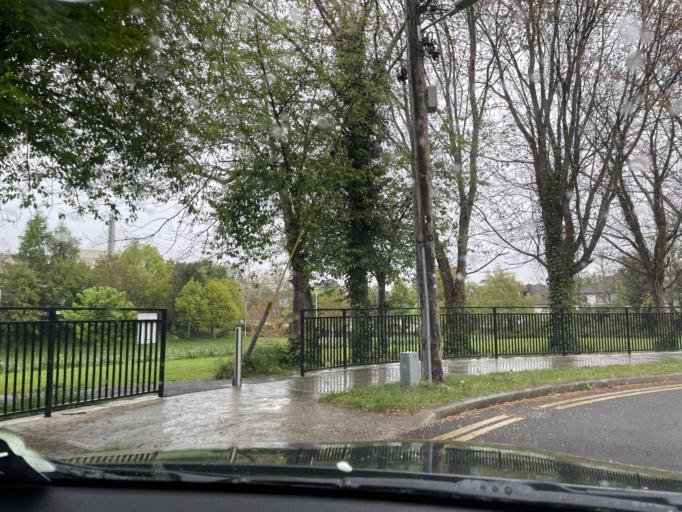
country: IE
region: Leinster
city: Dundrum
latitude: 53.2917
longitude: -6.2493
